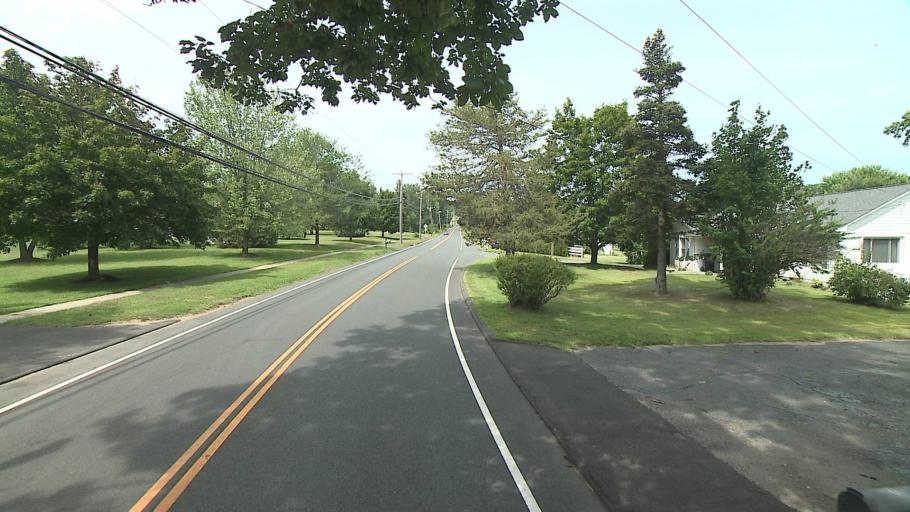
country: US
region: Connecticut
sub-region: Litchfield County
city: Plymouth
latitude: 41.6522
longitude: -73.0522
